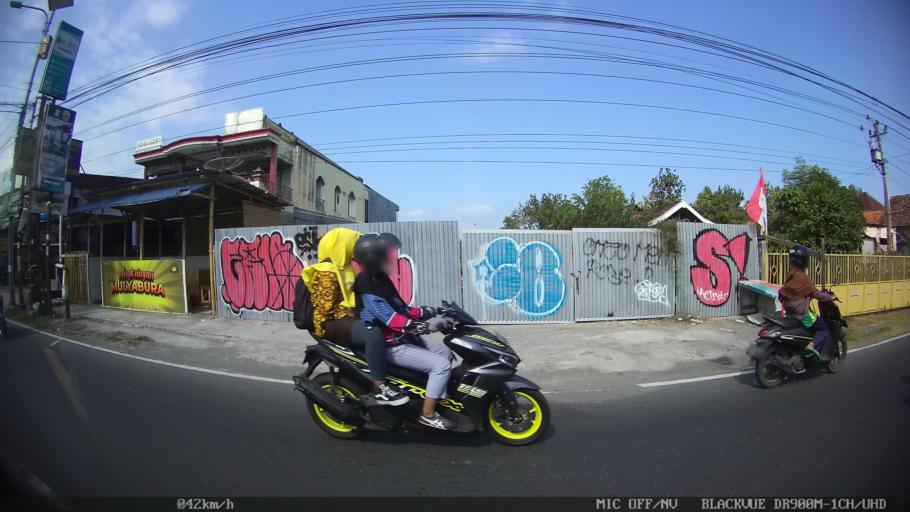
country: ID
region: Daerah Istimewa Yogyakarta
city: Sewon
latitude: -7.8547
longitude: 110.3901
